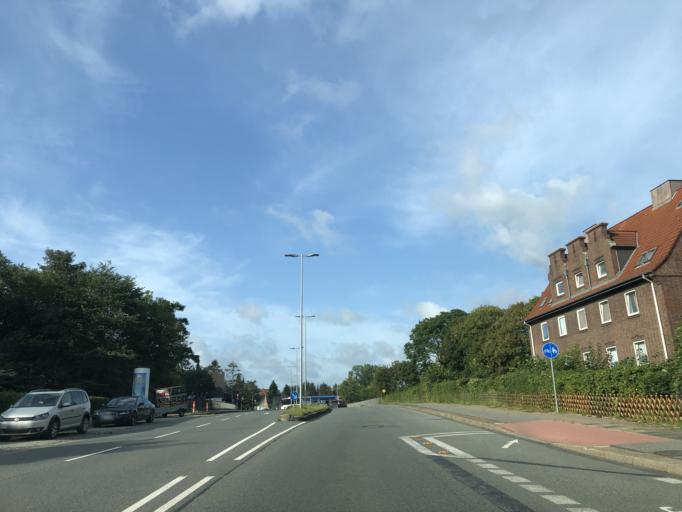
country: DE
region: Schleswig-Holstein
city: Flensburg
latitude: 54.7763
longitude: 9.4279
